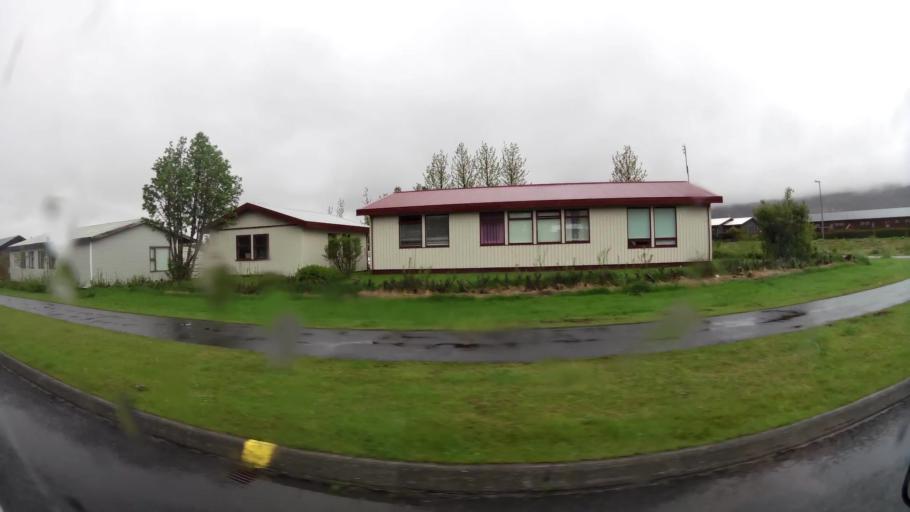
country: IS
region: South
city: Hveragerdi
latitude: 64.0028
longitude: -21.2015
